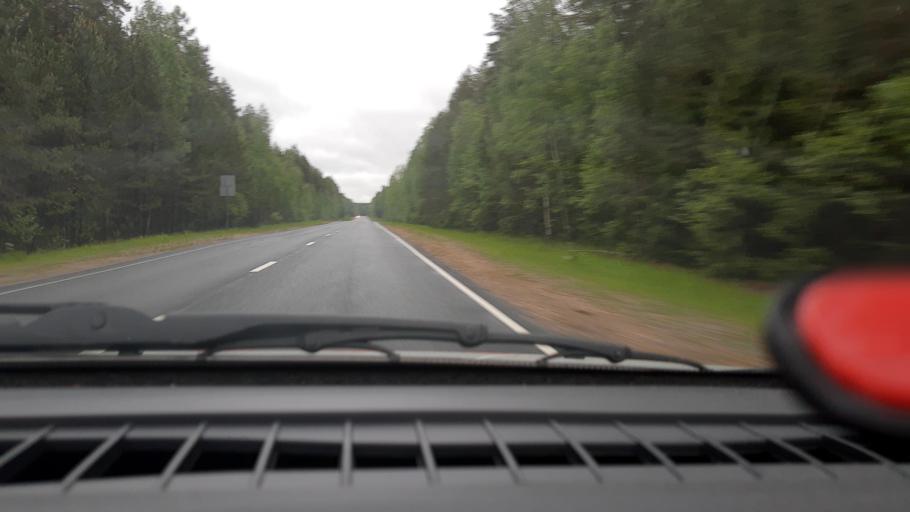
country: RU
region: Nizjnij Novgorod
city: Krasnyye Baki
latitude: 57.1671
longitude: 45.3105
